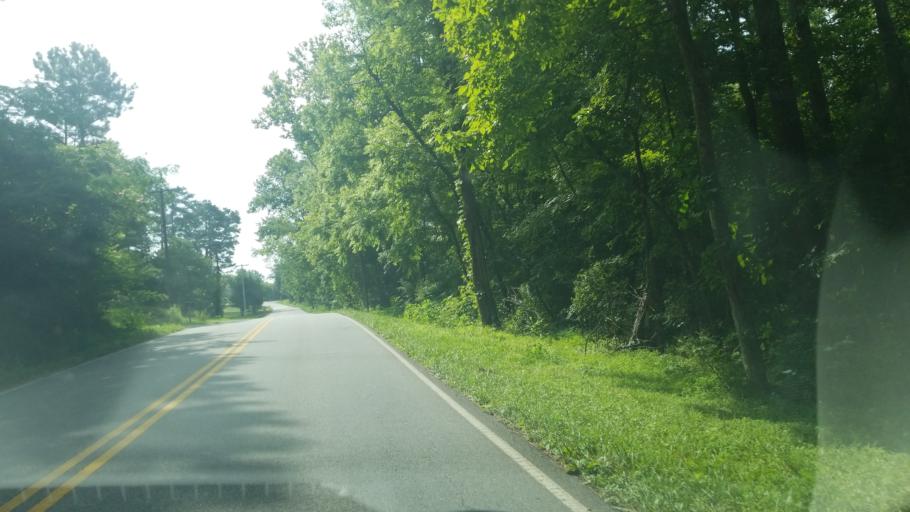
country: US
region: Tennessee
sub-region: Hamilton County
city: Apison
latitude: 35.0200
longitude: -85.0192
